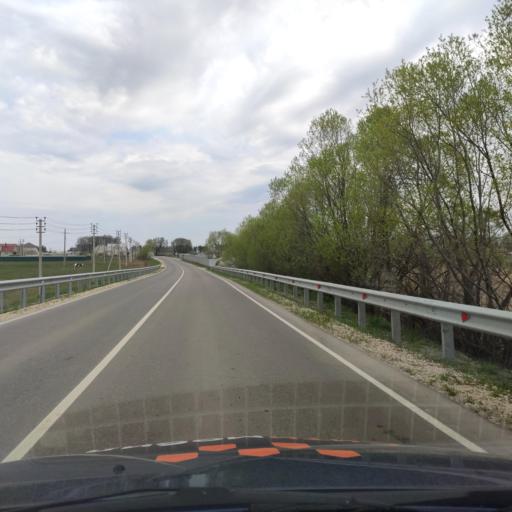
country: RU
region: Voronezj
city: Podgornoye
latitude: 51.8694
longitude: 39.1723
